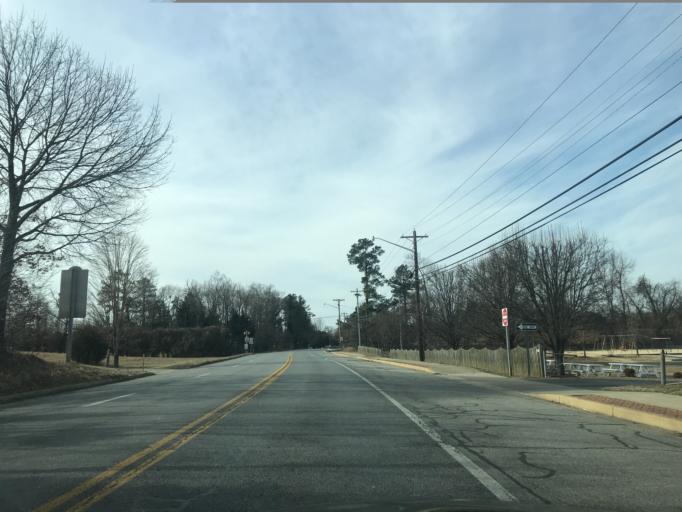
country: US
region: Maryland
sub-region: Charles County
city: La Plata
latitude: 38.5281
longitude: -76.9859
